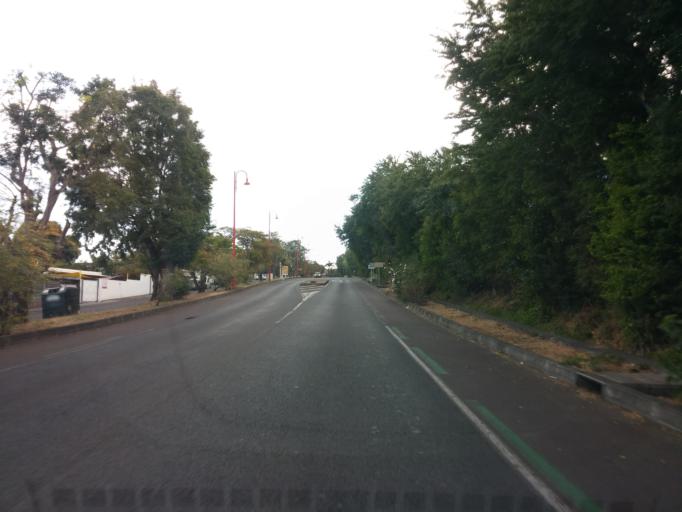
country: RE
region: Reunion
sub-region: Reunion
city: La Possession
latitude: -20.9381
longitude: 55.3321
